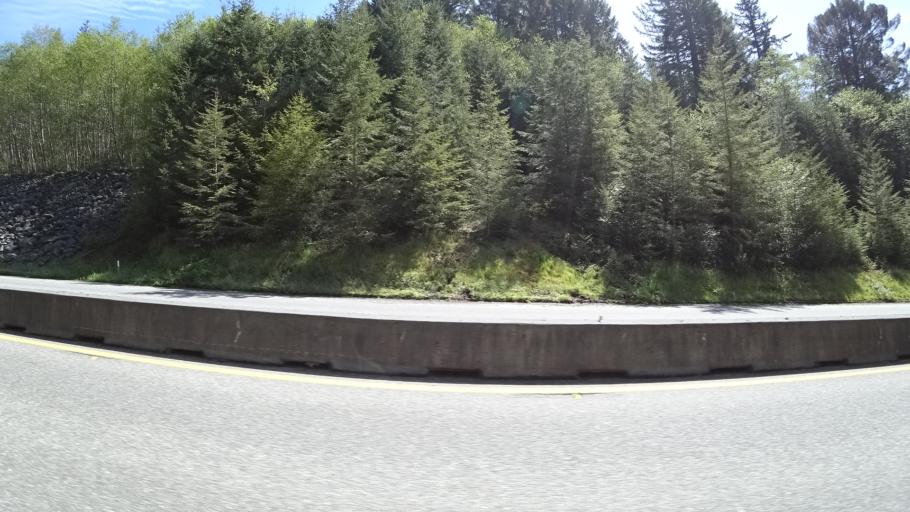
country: US
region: California
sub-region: Humboldt County
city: Westhaven-Moonstone
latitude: 41.3837
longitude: -123.9950
